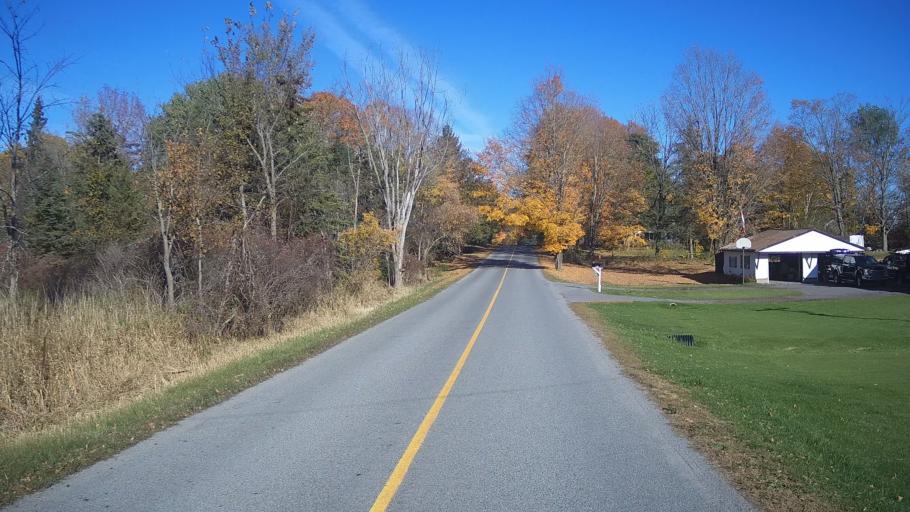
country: CA
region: Ontario
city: Kingston
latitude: 44.4484
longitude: -76.5145
